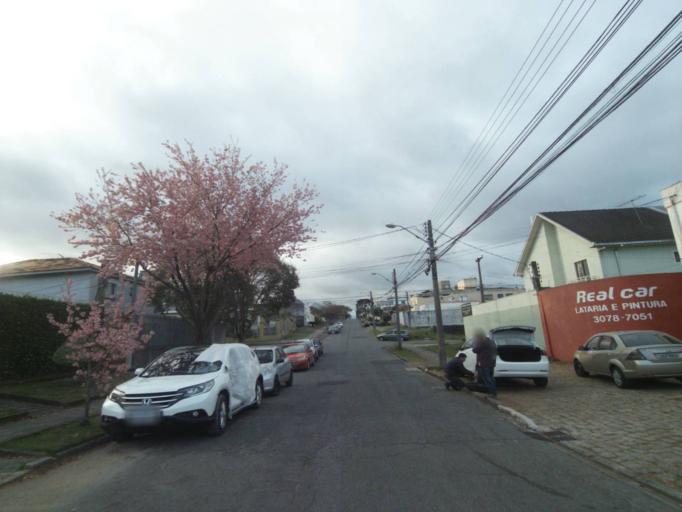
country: BR
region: Parana
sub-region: Curitiba
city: Curitiba
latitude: -25.4575
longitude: -49.2624
